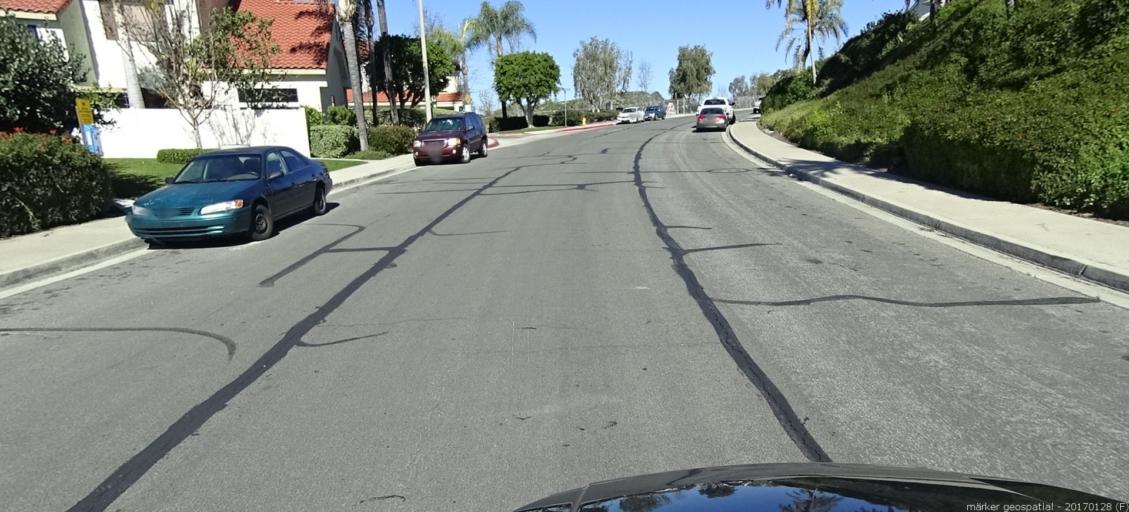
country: US
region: California
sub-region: Orange County
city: Lake Forest
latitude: 33.6575
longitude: -117.6895
